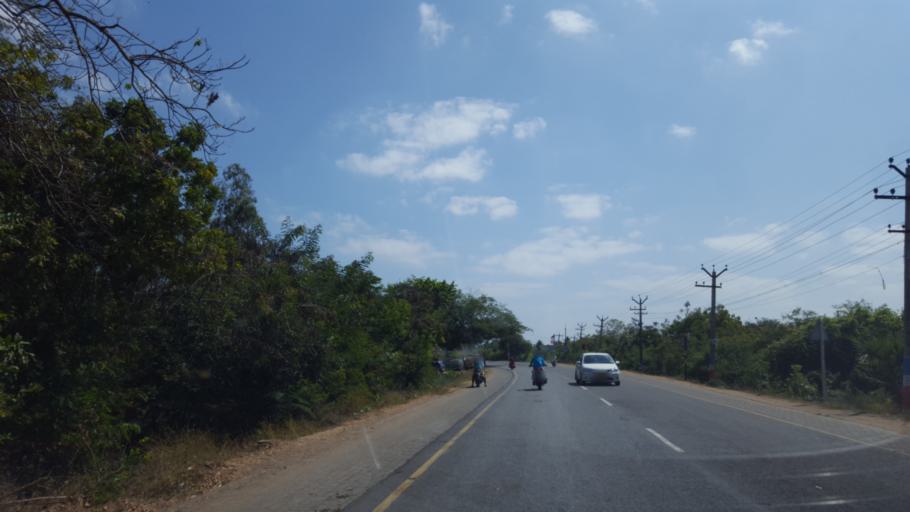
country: IN
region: Tamil Nadu
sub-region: Kancheepuram
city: Mamallapuram
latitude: 12.6148
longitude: 80.1707
